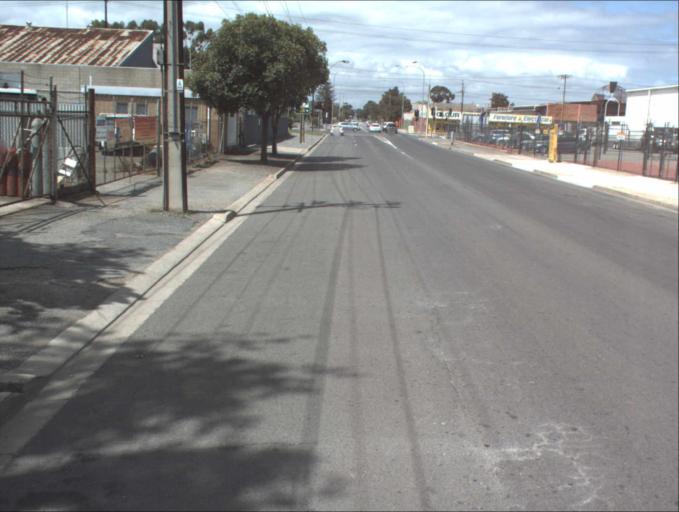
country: AU
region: South Australia
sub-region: Port Adelaide Enfield
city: Enfield
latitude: -34.8474
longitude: 138.5913
